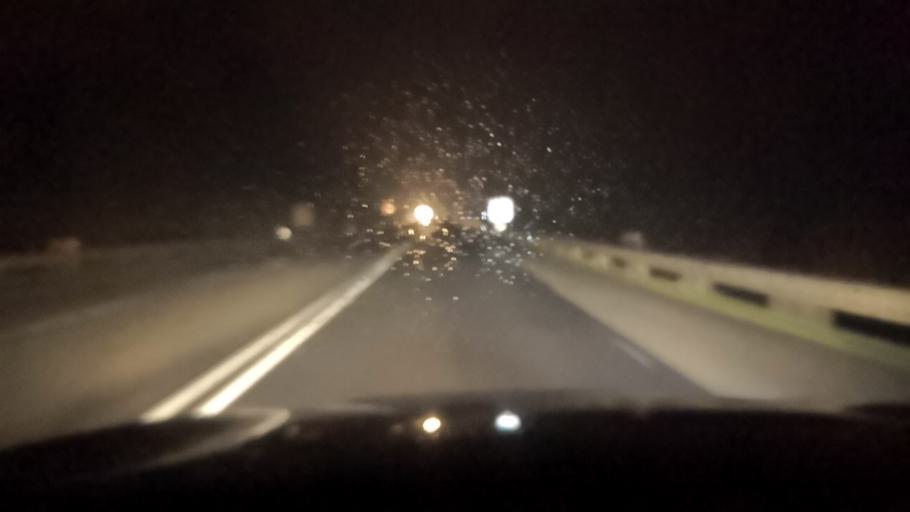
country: PT
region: Viseu
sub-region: Santa Comba Dao
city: Santa Comba Dao
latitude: 40.4253
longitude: -8.1178
